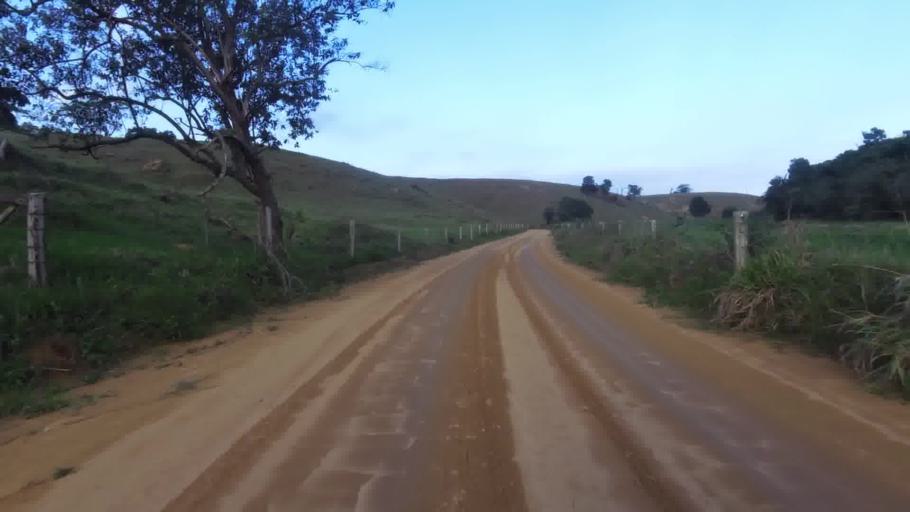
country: BR
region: Espirito Santo
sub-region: Alfredo Chaves
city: Alfredo Chaves
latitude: -20.6994
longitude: -40.6390
